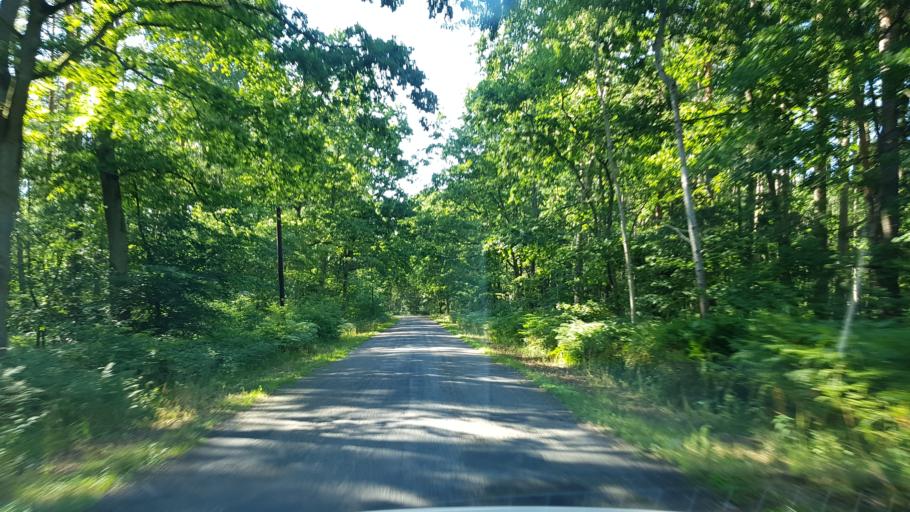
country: PL
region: West Pomeranian Voivodeship
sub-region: Powiat goleniowski
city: Goleniow
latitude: 53.5527
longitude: 14.7725
